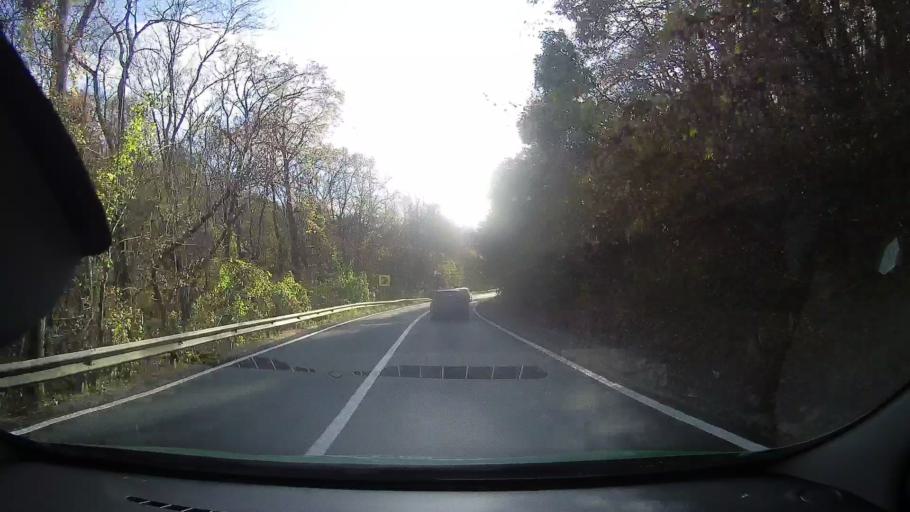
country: RO
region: Tulcea
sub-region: Comuna Topolog
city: Topolog
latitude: 44.9155
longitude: 28.4210
